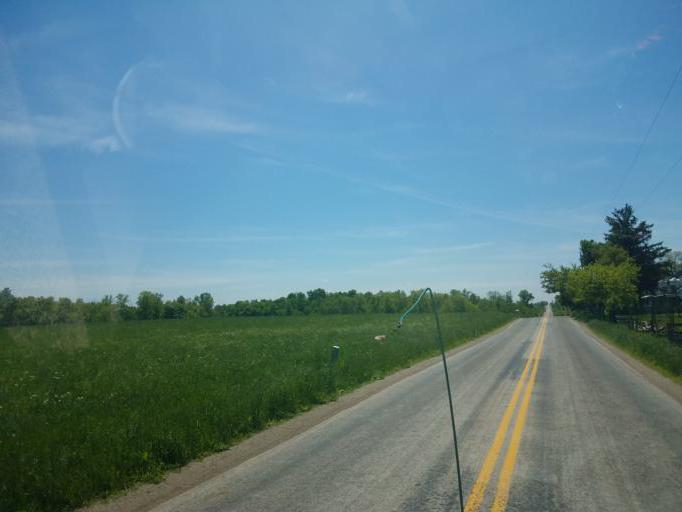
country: US
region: Ohio
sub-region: Ashland County
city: Ashland
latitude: 40.9472
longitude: -82.2436
